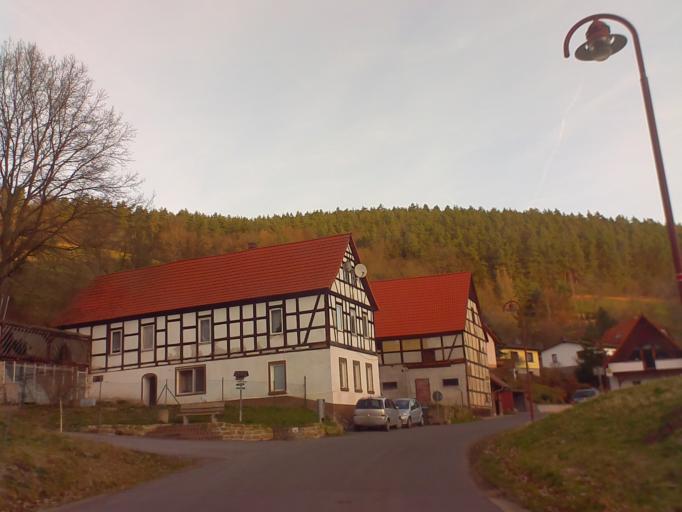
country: DE
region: Thuringia
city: Hummelshain
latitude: 50.7391
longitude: 11.6161
